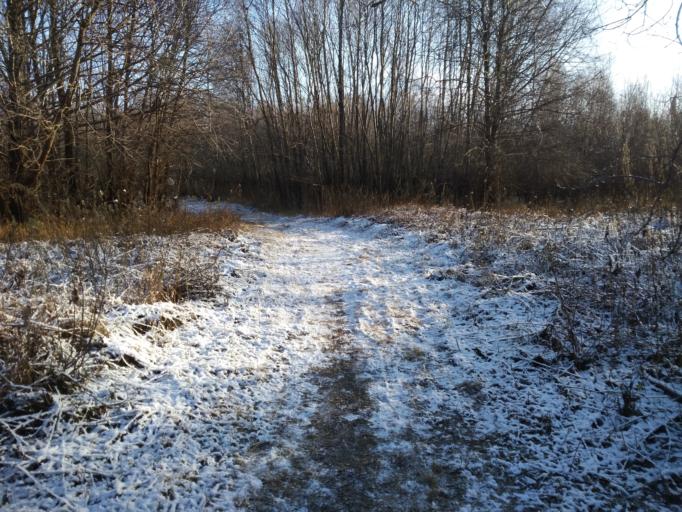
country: RU
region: Kirov
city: Vyatskiye Polyany
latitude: 56.2368
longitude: 51.0800
